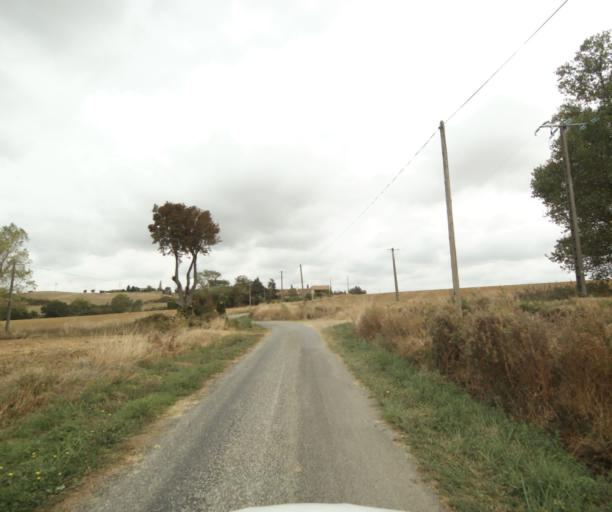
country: FR
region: Midi-Pyrenees
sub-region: Departement de la Haute-Garonne
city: Villefranche-de-Lauragais
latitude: 43.4131
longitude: 1.7273
